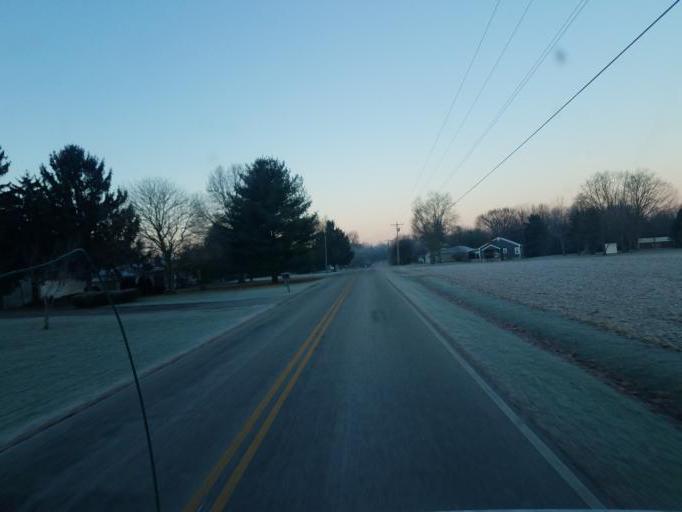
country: US
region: Ohio
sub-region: Marion County
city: Marion
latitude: 40.5153
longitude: -83.0381
